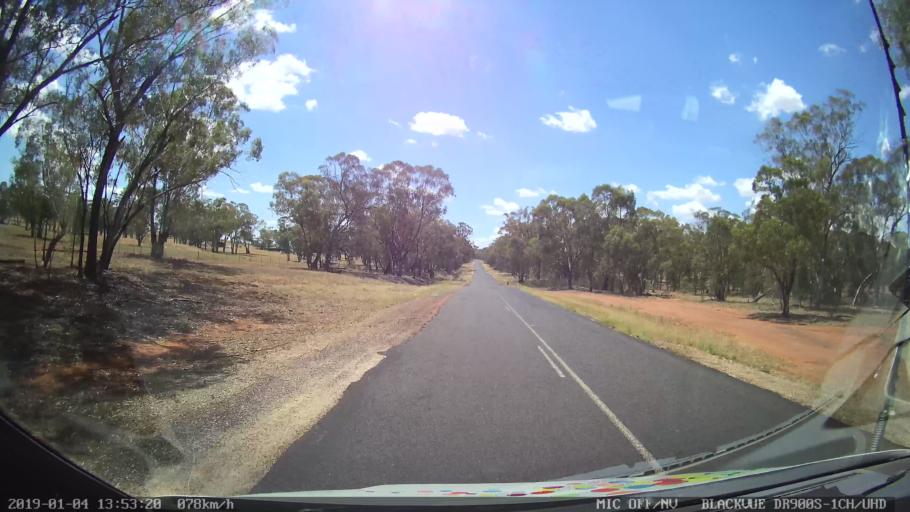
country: AU
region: New South Wales
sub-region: Dubbo Municipality
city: Dubbo
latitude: -32.3842
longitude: 148.5737
